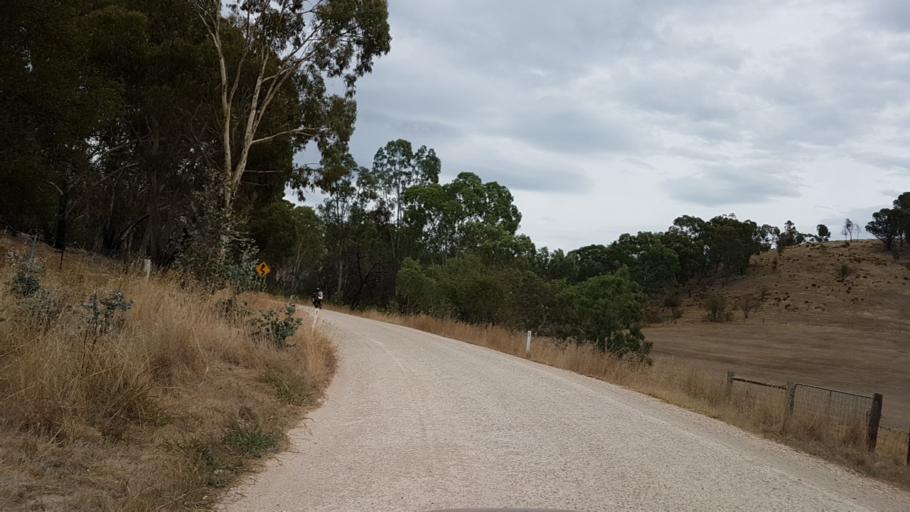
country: AU
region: South Australia
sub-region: Adelaide Hills
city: Gumeracha
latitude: -34.8012
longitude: 138.8299
